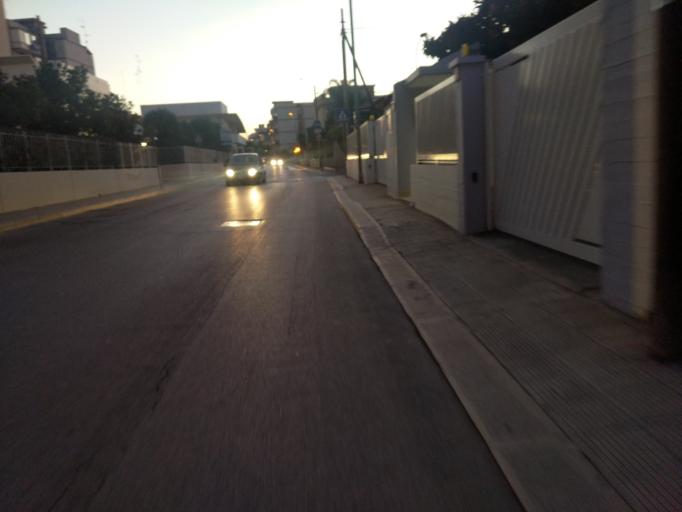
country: IT
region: Apulia
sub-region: Provincia di Bari
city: Modugno
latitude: 41.0772
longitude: 16.7854
